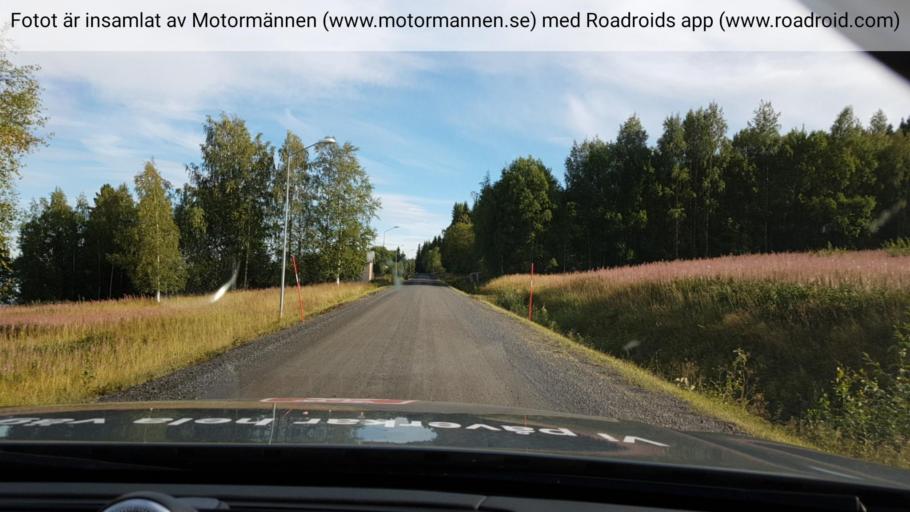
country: SE
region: Jaemtland
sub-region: Stroemsunds Kommun
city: Stroemsund
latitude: 64.1129
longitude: 15.8137
